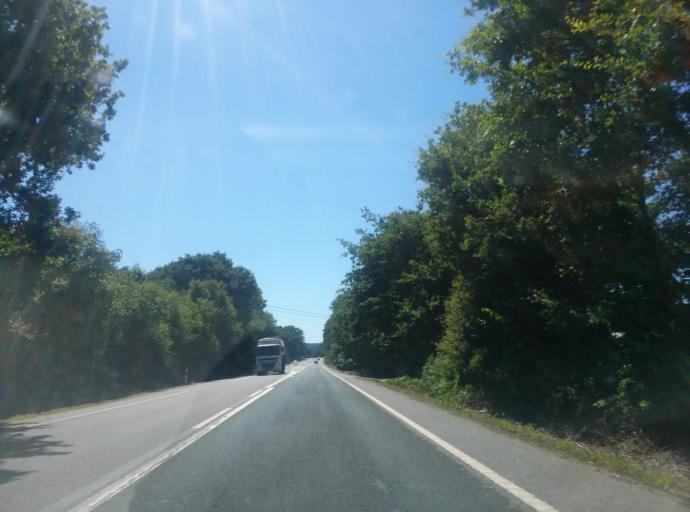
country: ES
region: Galicia
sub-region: Provincia de Lugo
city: Castro de Rei
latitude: 43.1163
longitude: -7.4424
